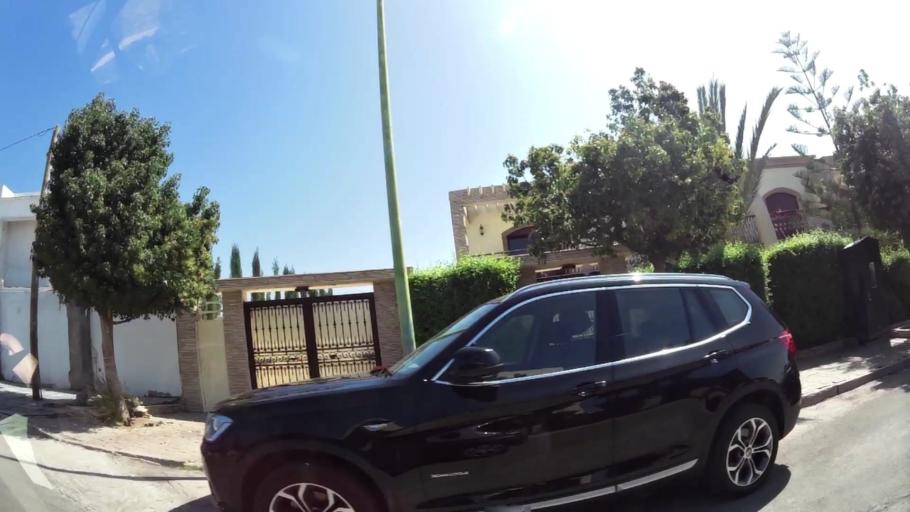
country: MA
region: Souss-Massa-Draa
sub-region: Agadir-Ida-ou-Tnan
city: Agadir
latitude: 30.4427
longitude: -9.5944
